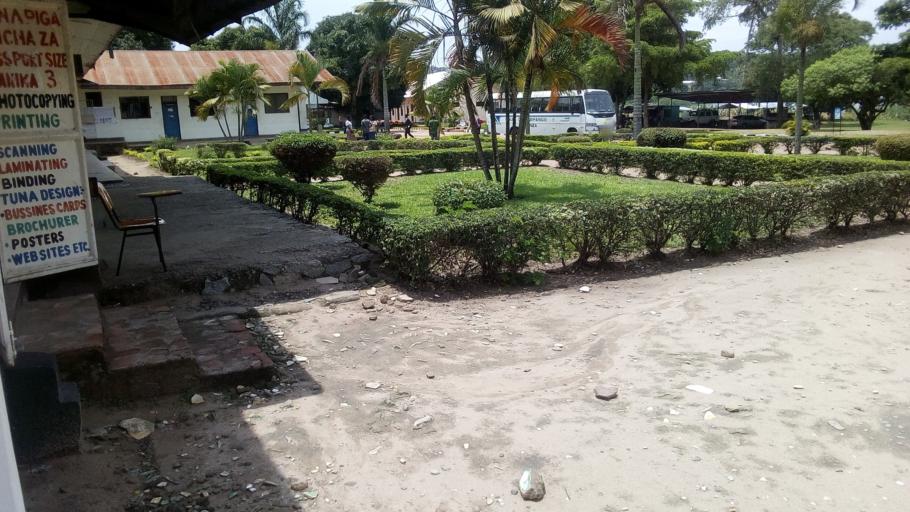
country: TZ
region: Mwanza
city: Mwanza
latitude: -2.4731
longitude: 32.8981
